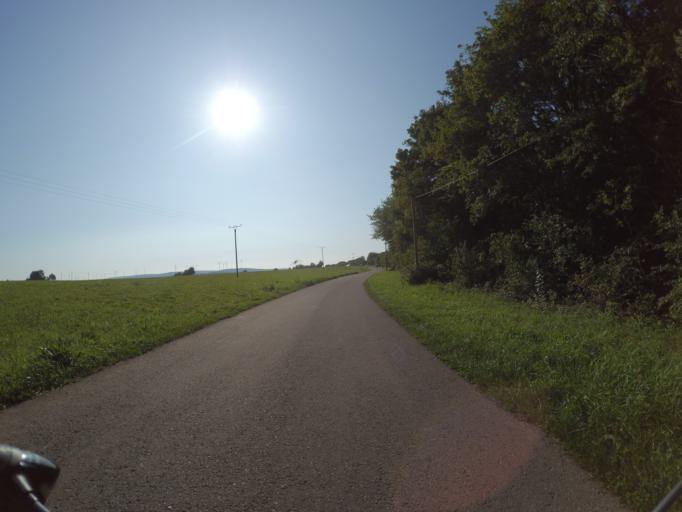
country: DE
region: Rheinland-Pfalz
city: Trittenheim
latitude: 49.8452
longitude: 6.9050
